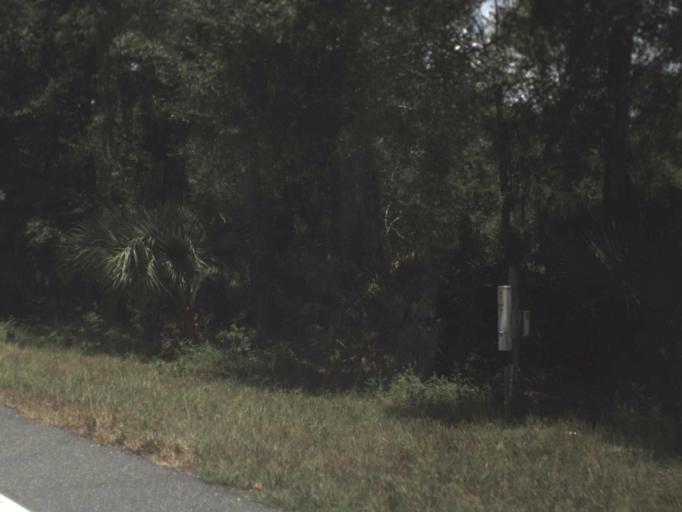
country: US
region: Florida
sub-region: Taylor County
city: Perry
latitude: 30.1414
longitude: -83.8739
